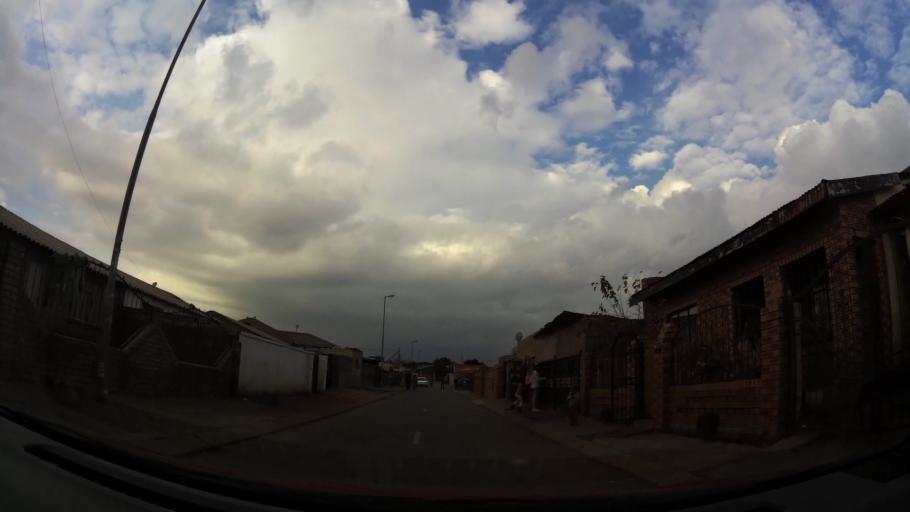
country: ZA
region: Gauteng
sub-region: City of Johannesburg Metropolitan Municipality
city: Soweto
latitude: -26.2442
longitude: 27.8207
